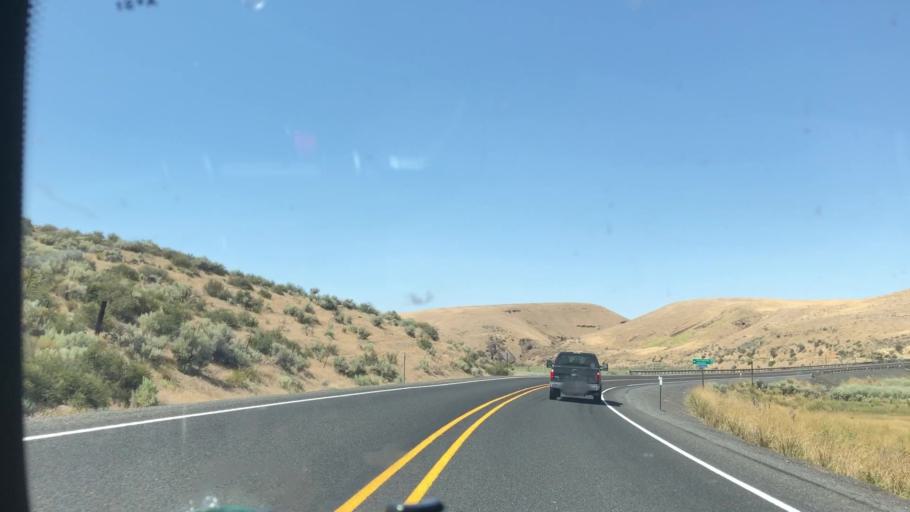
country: US
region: Idaho
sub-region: Owyhee County
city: Marsing
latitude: 43.2261
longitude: -117.0539
